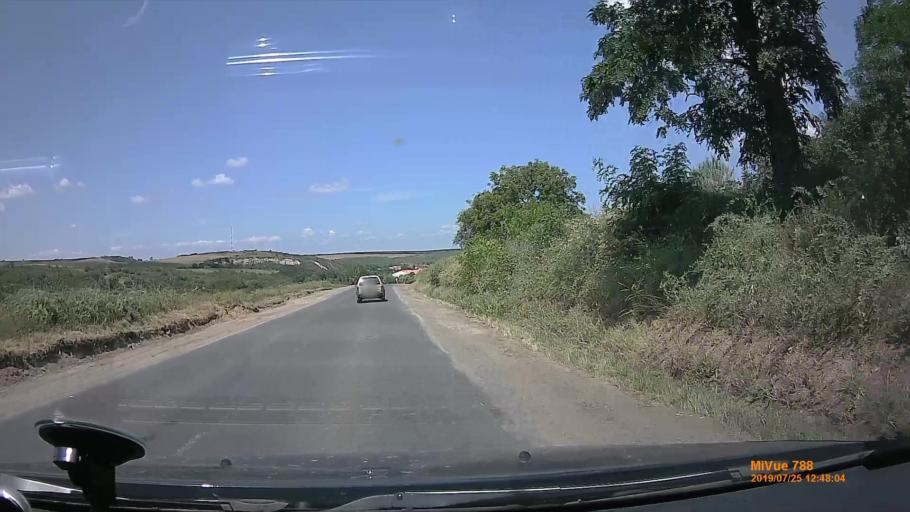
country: HU
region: Borsod-Abauj-Zemplen
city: Abaujszanto
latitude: 48.2661
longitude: 21.1842
